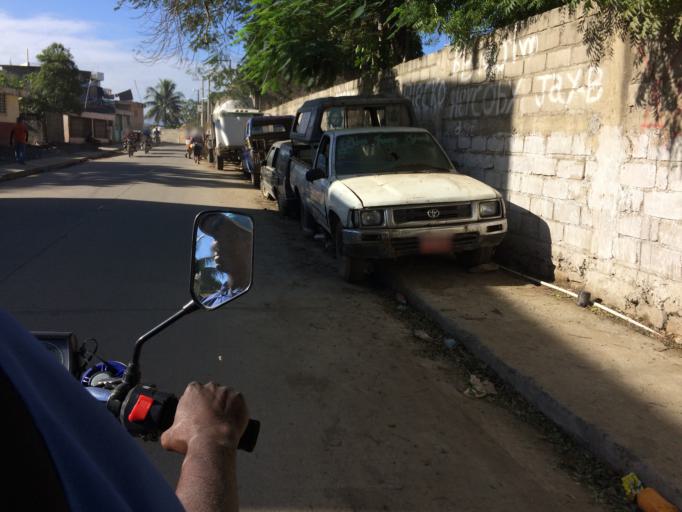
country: HT
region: Nord
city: Okap
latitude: 19.7491
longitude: -72.2161
